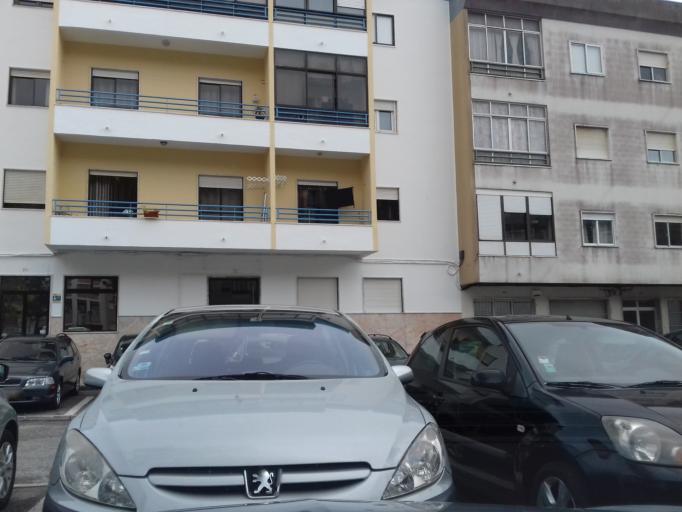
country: PT
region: Lisbon
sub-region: Sintra
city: Queluz
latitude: 38.7604
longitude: -9.2451
